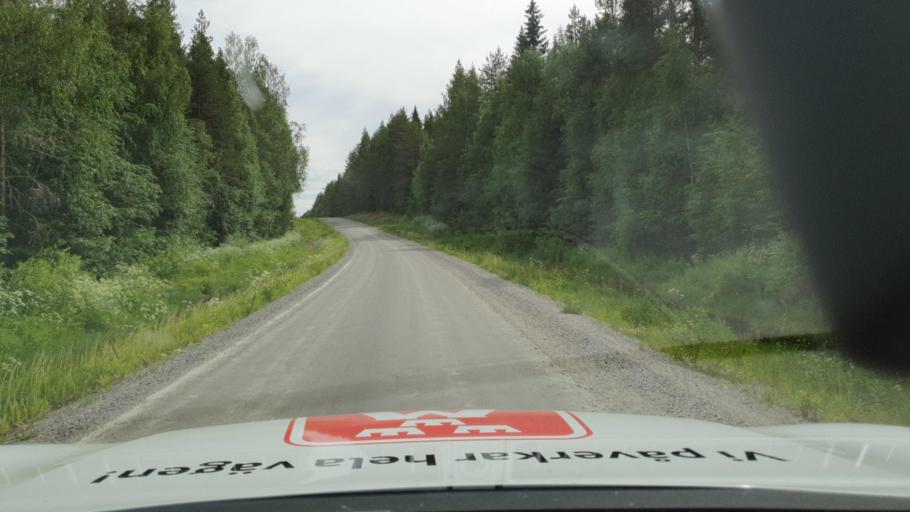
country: SE
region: Vaesterbotten
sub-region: Skelleftea Kommun
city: Burea
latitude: 64.4407
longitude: 21.0176
